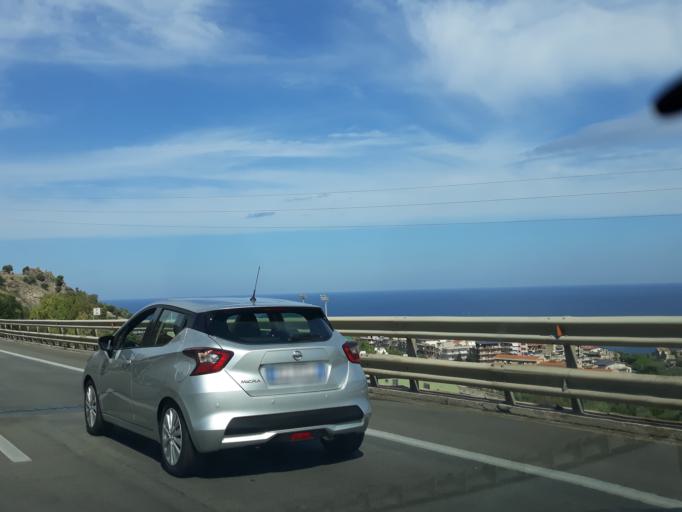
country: IT
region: Sicily
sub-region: Palermo
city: Trabia
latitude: 37.9854
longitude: 13.6573
